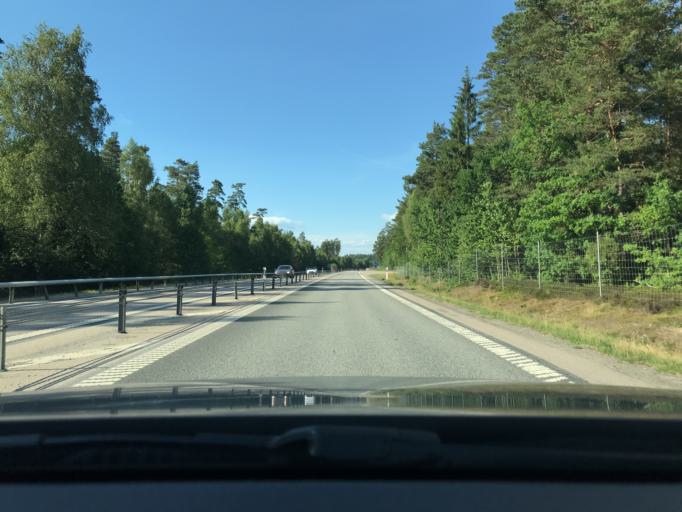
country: SE
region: Skane
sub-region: Osby Kommun
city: Osby
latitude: 56.3948
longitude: 14.0370
